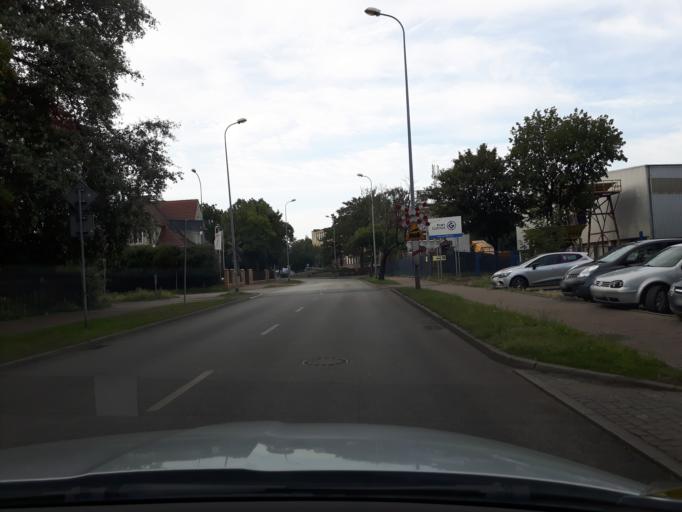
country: PL
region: Pomeranian Voivodeship
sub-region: Gdynia
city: Gdynia
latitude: 54.5289
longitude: 18.5429
